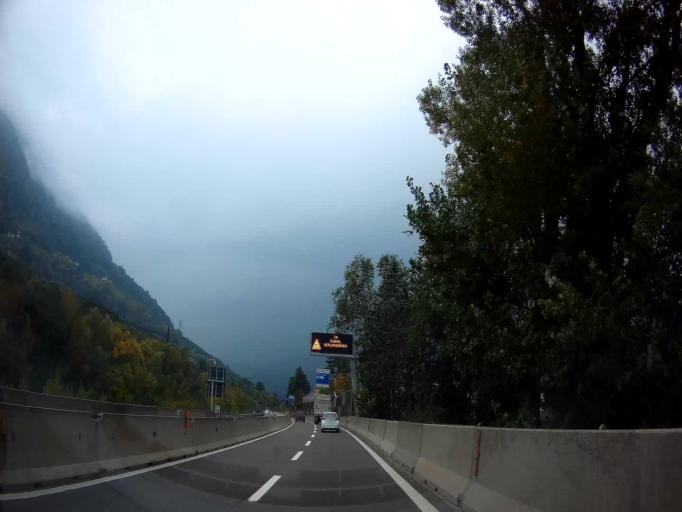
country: IT
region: Trentino-Alto Adige
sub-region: Bolzano
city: Marlengo
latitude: 46.6649
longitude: 11.1434
